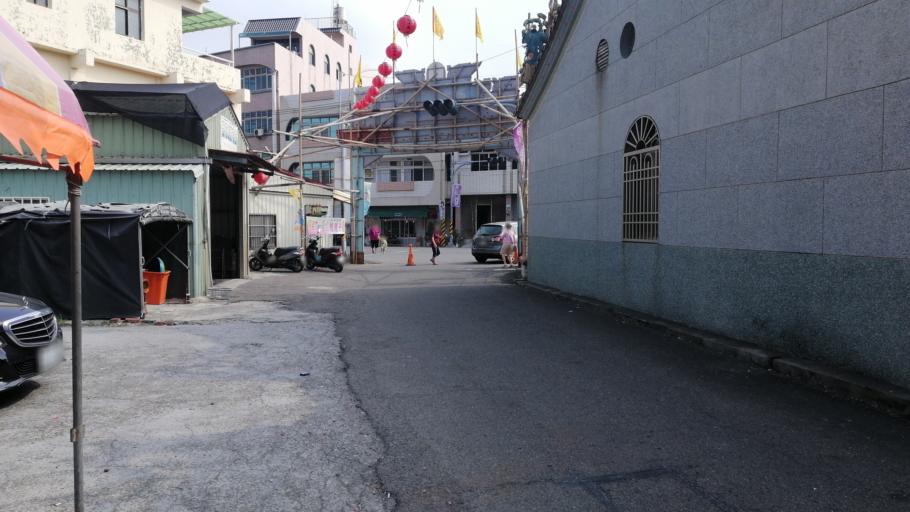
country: TW
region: Taiwan
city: Xinying
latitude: 23.3859
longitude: 120.1707
